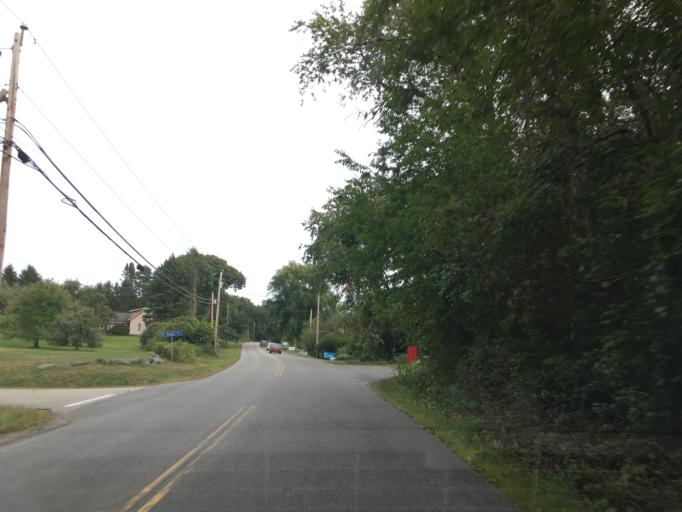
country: US
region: New Hampshire
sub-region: Rockingham County
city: Exeter
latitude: 42.9894
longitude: -70.9162
